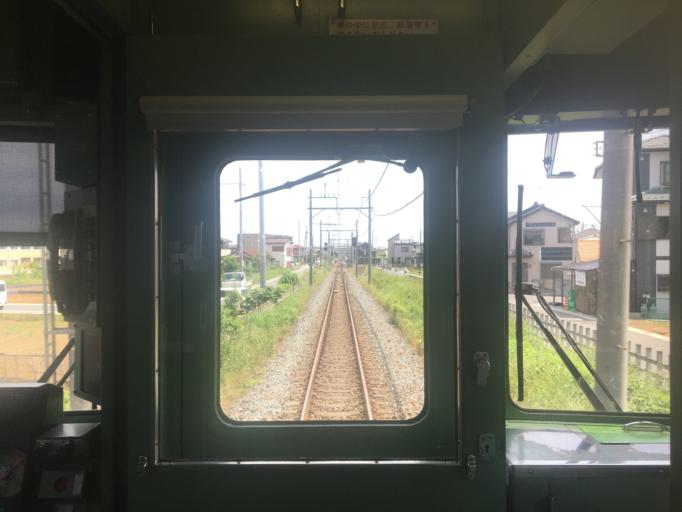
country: JP
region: Saitama
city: Sakado
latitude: 35.9382
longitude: 139.3674
